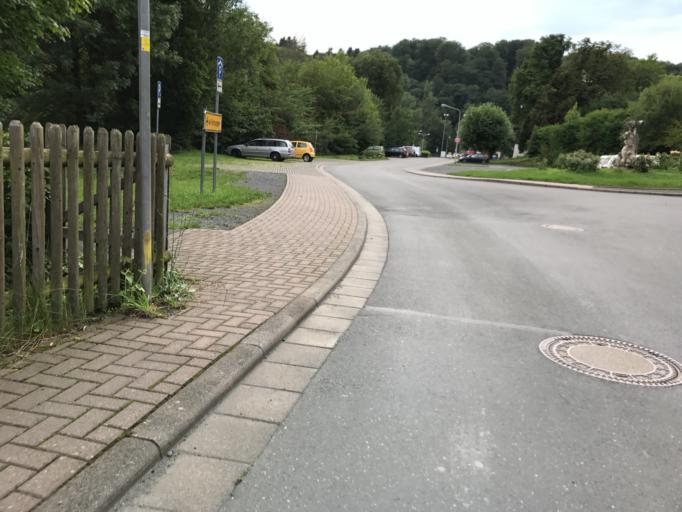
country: DE
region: Hesse
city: Weilburg
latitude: 50.4830
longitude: 8.2612
